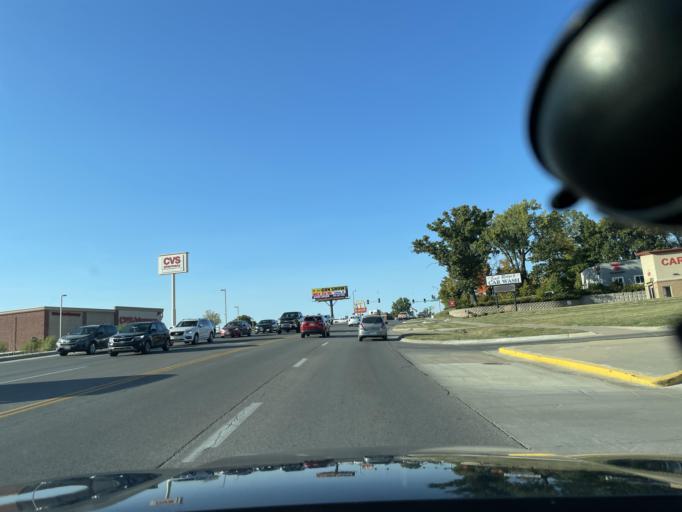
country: US
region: Missouri
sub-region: Andrew County
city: Country Club Village
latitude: 39.7996
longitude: -94.8147
